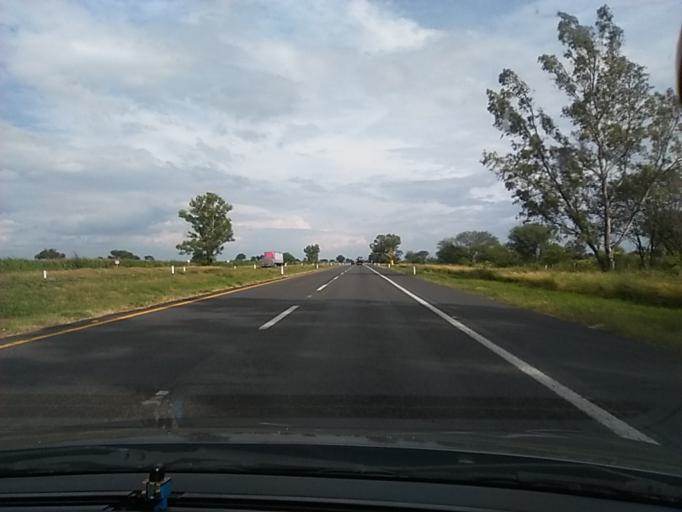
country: MX
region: Jalisco
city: La Barca
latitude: 20.3440
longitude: -102.6181
